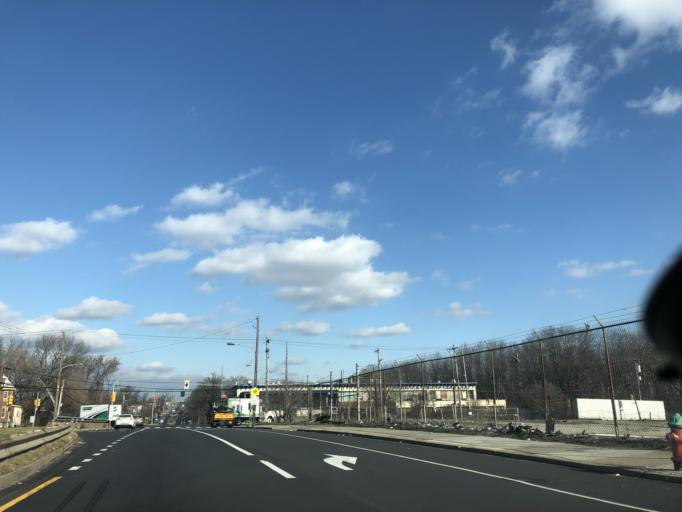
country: US
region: Pennsylvania
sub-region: Delaware County
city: Colwyn
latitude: 39.9273
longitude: -75.2198
